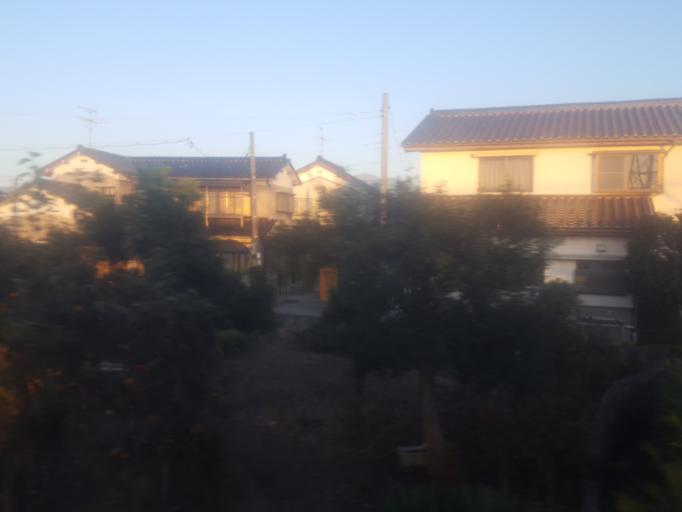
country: JP
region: Toyama
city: Kamiichi
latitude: 36.6852
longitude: 137.3177
